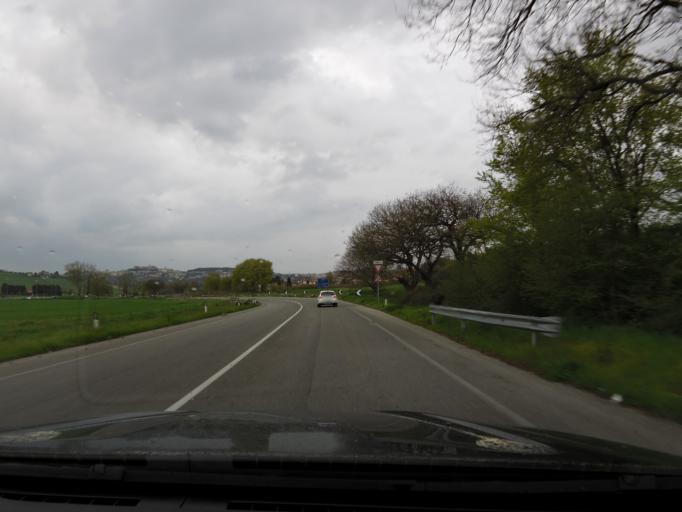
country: IT
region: The Marches
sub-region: Provincia di Ancona
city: Villa Musone
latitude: 43.4578
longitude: 13.5873
